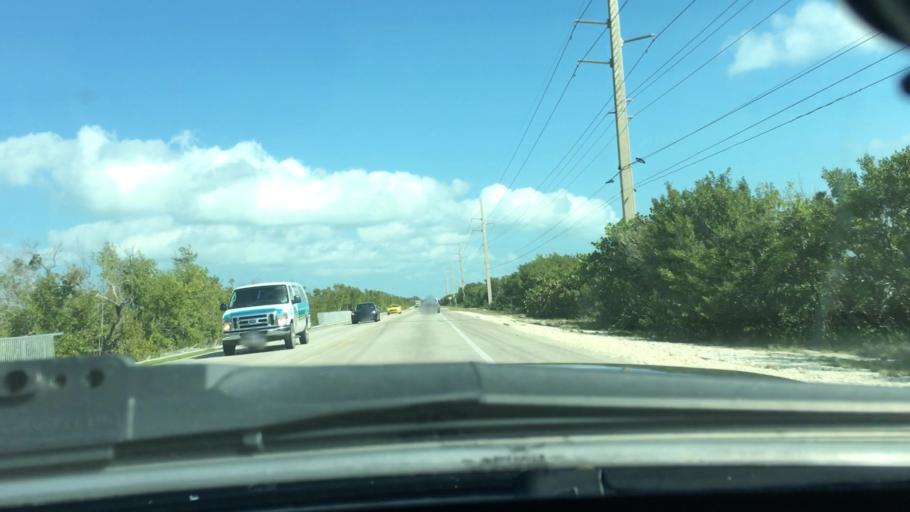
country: US
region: Florida
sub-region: Monroe County
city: Big Pine Key
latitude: 24.6668
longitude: -81.2593
